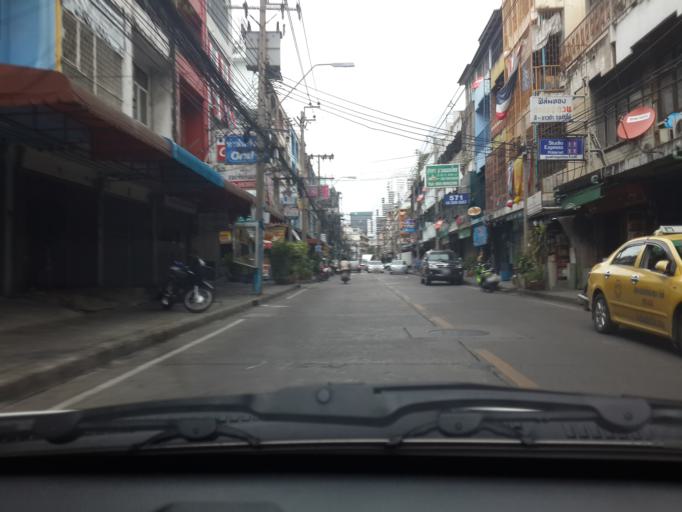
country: TH
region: Bangkok
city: Khlong Toei
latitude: 13.7226
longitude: 100.5647
